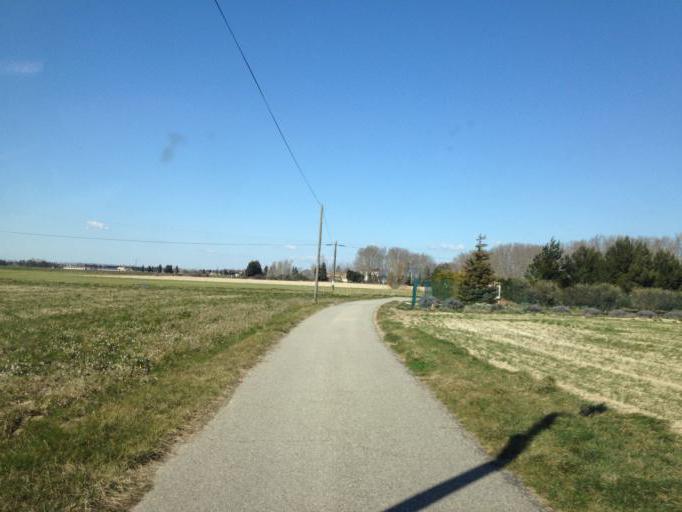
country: FR
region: Provence-Alpes-Cote d'Azur
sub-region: Departement du Vaucluse
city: Bedarrides
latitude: 44.0443
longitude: 4.9231
